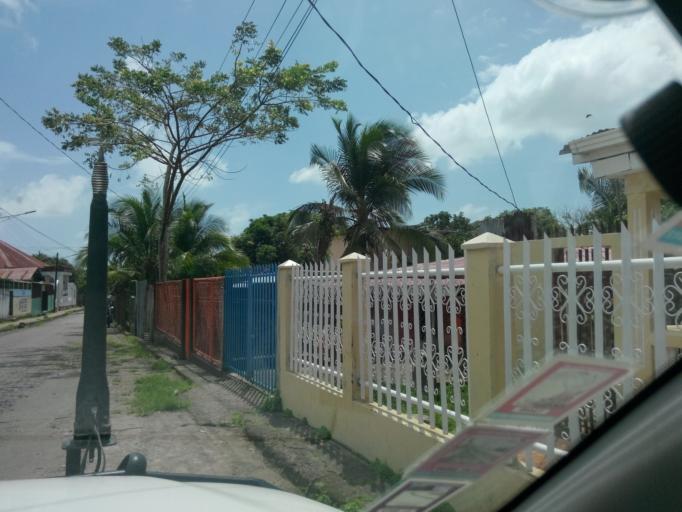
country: NI
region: Atlantico Sur
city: Bluefields
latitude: 12.0140
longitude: -83.7615
